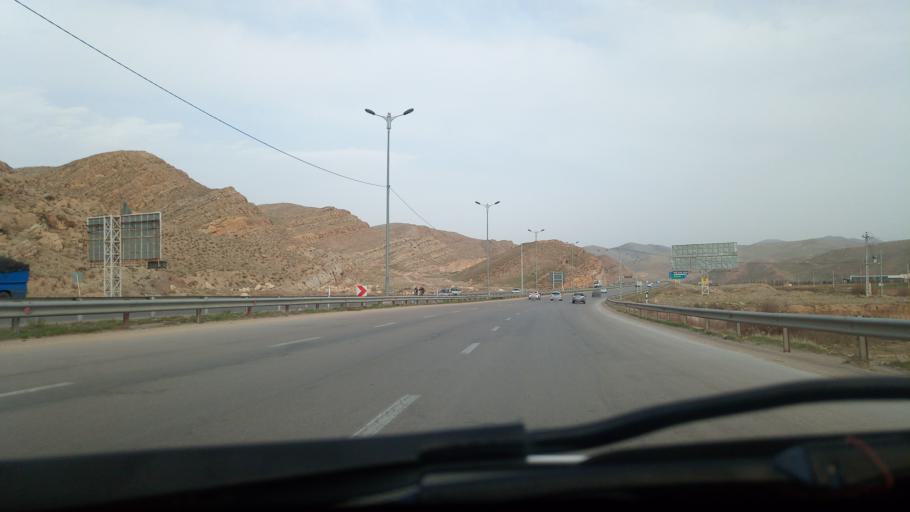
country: IR
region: Khorasan-e Shomali
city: Bojnurd
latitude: 37.4803
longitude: 57.4082
